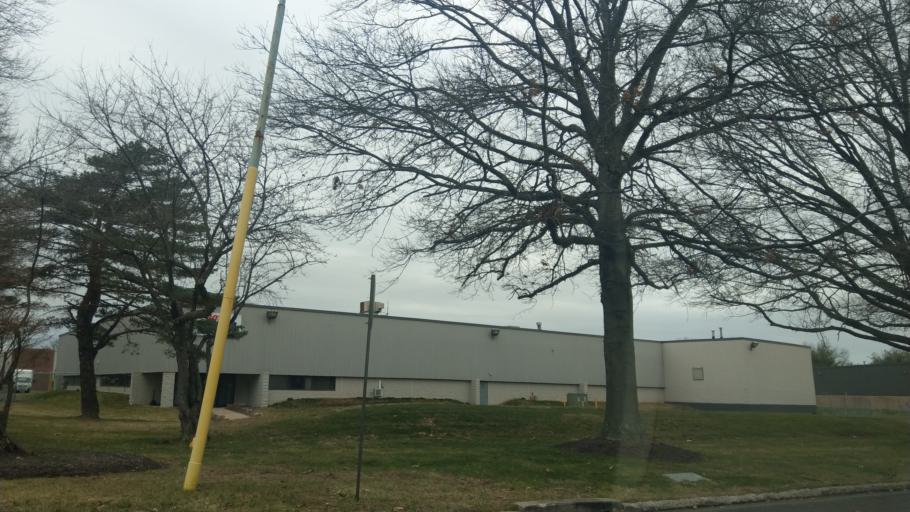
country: US
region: Pennsylvania
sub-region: Bucks County
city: Hulmeville
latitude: 40.1195
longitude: -74.8911
